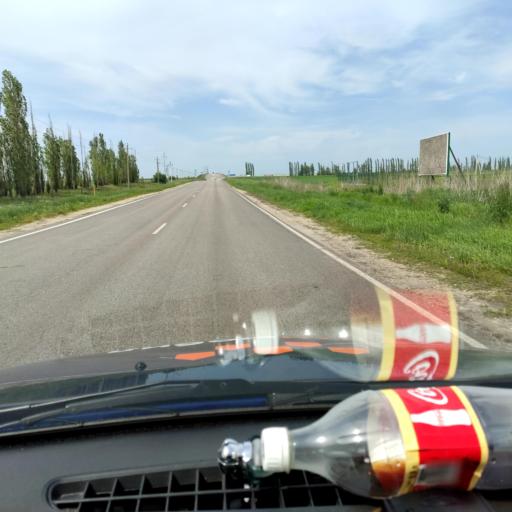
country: RU
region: Voronezj
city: Novaya Usman'
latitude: 51.5821
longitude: 39.3747
